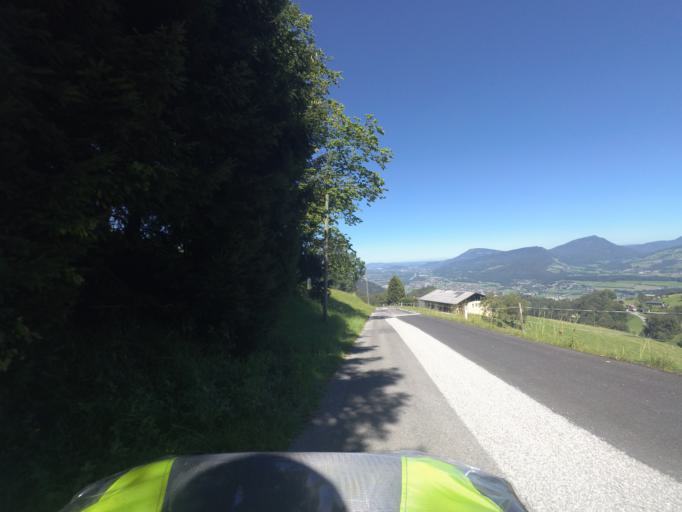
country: AT
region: Salzburg
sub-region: Politischer Bezirk Hallein
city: Hallein
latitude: 47.6562
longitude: 13.0962
